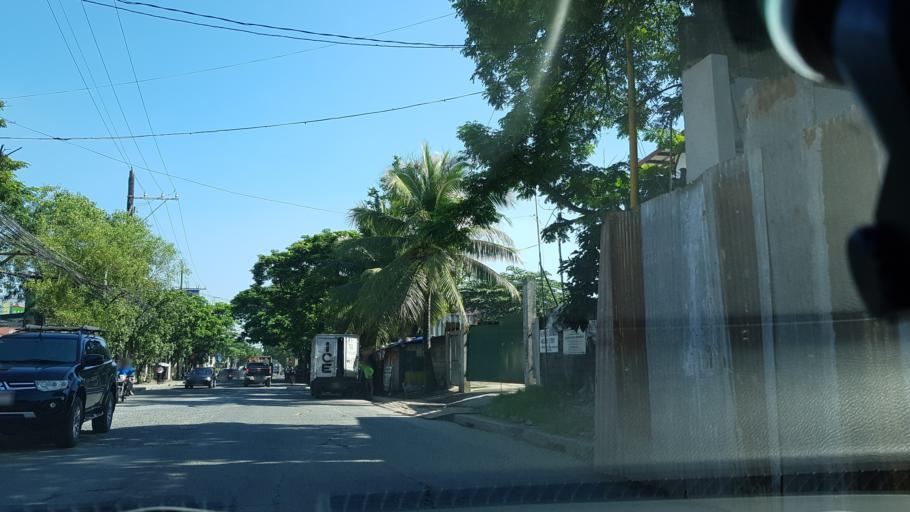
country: PH
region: Calabarzon
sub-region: Province of Rizal
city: Cainta
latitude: 14.5638
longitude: 121.0939
